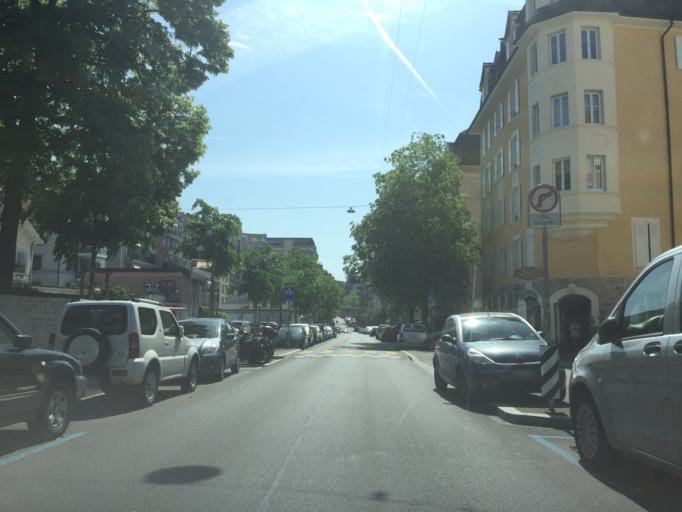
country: CH
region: Vaud
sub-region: Lausanne District
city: Lausanne
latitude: 46.5149
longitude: 6.6264
